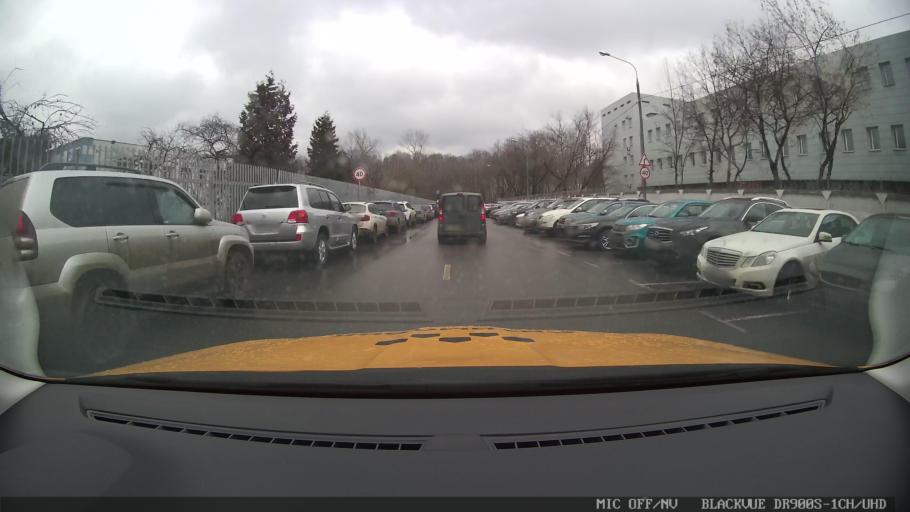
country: RU
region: Moscow
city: Vatutino
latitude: 55.8630
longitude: 37.7007
